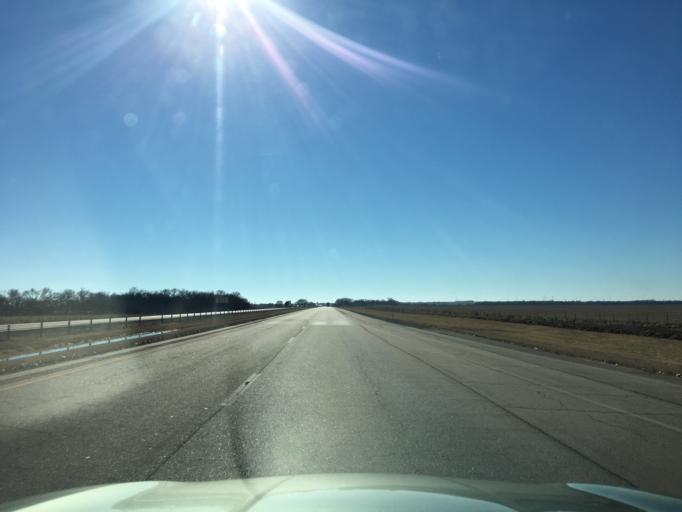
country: US
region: Oklahoma
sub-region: Kay County
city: Blackwell
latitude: 36.9245
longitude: -97.3498
